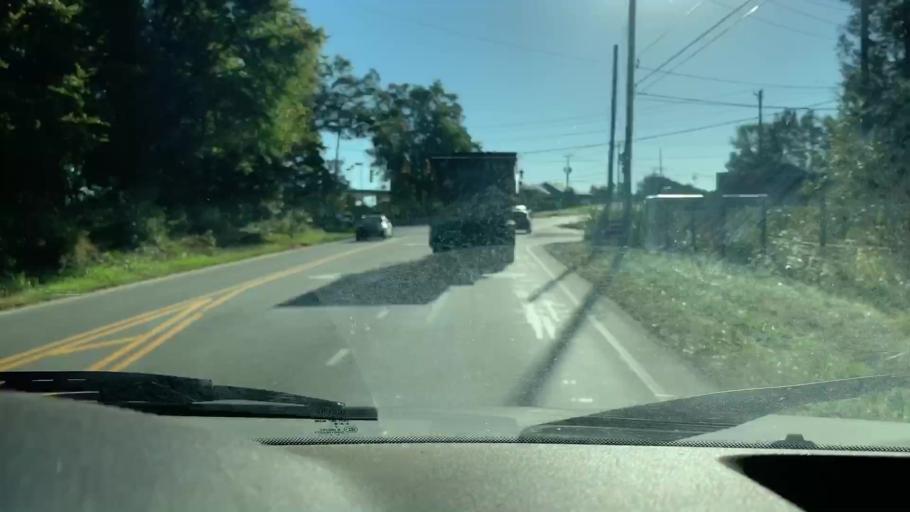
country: US
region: North Carolina
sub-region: Mecklenburg County
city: Huntersville
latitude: 35.4187
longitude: -80.7465
